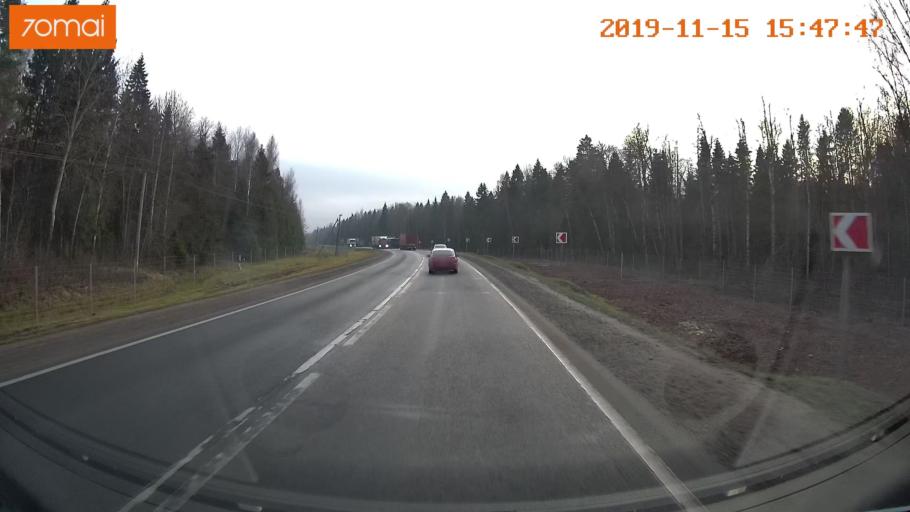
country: RU
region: Jaroslavl
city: Danilov
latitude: 57.9346
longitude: 40.0070
